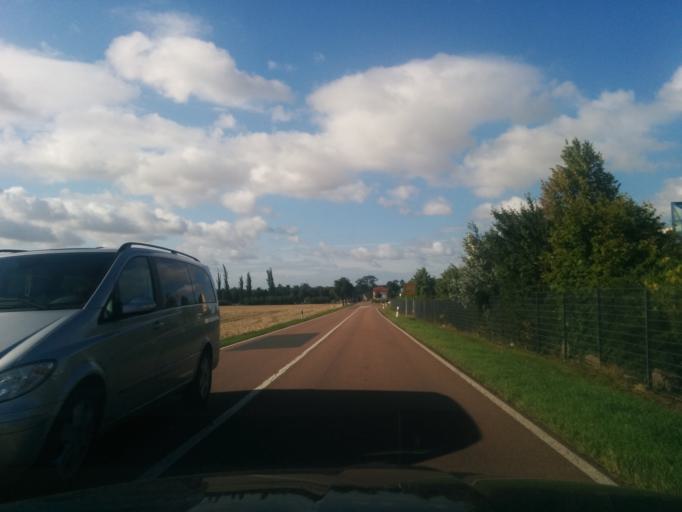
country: DE
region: Saxony-Anhalt
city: Bennstedt
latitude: 51.4704
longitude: 11.8218
